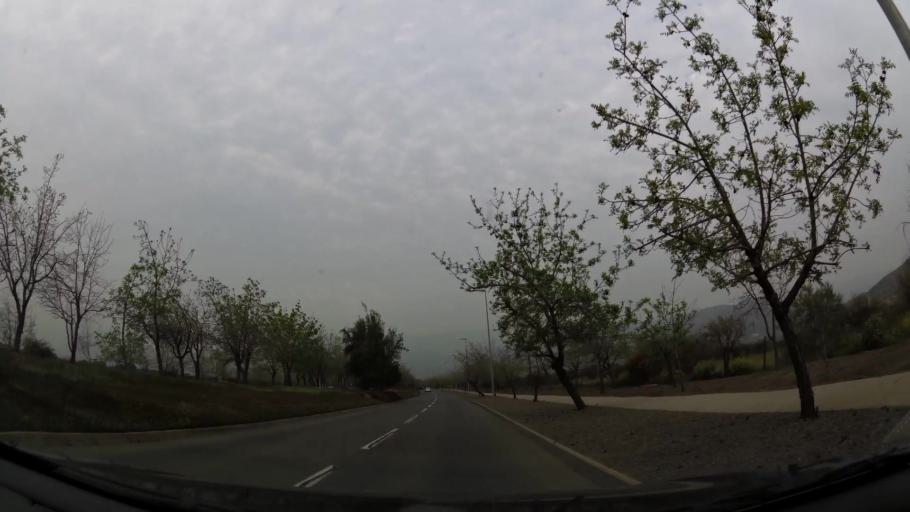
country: CL
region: Santiago Metropolitan
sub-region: Provincia de Chacabuco
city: Chicureo Abajo
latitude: -33.2839
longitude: -70.6493
